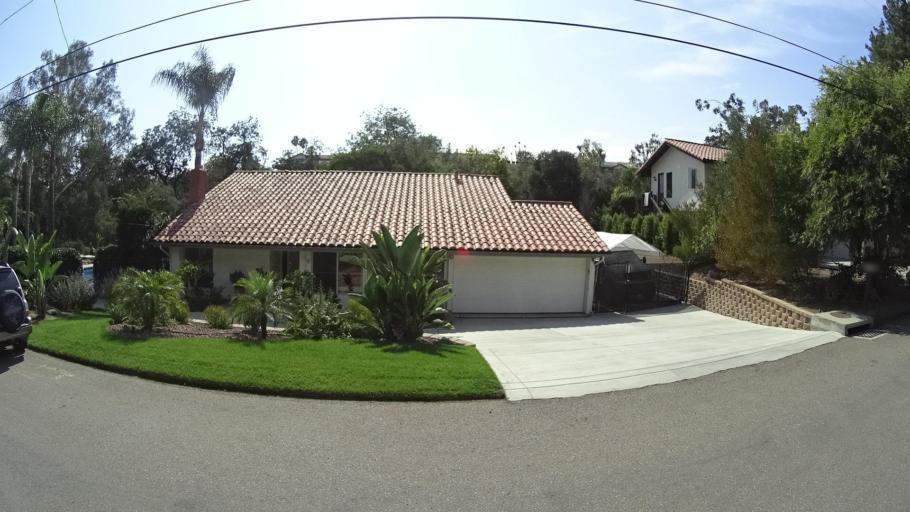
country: US
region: California
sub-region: San Diego County
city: Escondido
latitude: 33.0878
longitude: -117.0621
